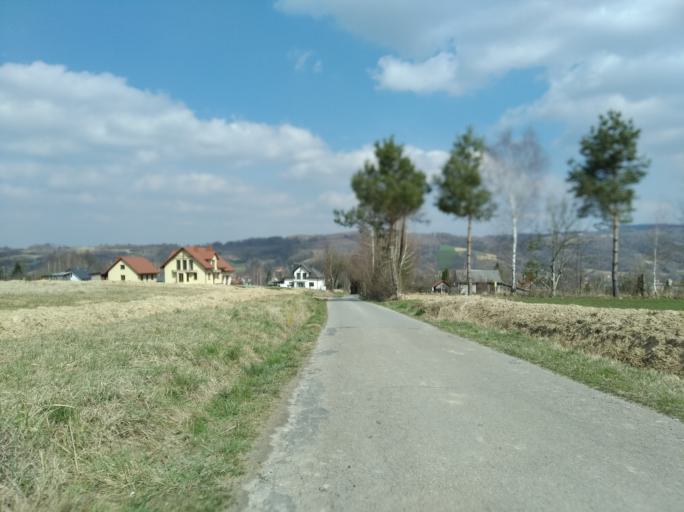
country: PL
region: Subcarpathian Voivodeship
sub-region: Powiat strzyzowski
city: Strzyzow
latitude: 49.8384
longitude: 21.8090
